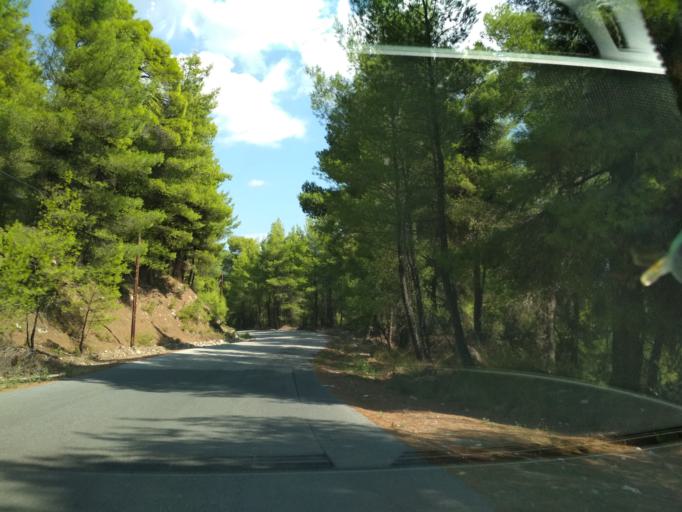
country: GR
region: Central Greece
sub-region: Nomos Evvoias
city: Roviai
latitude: 38.8191
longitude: 23.2773
